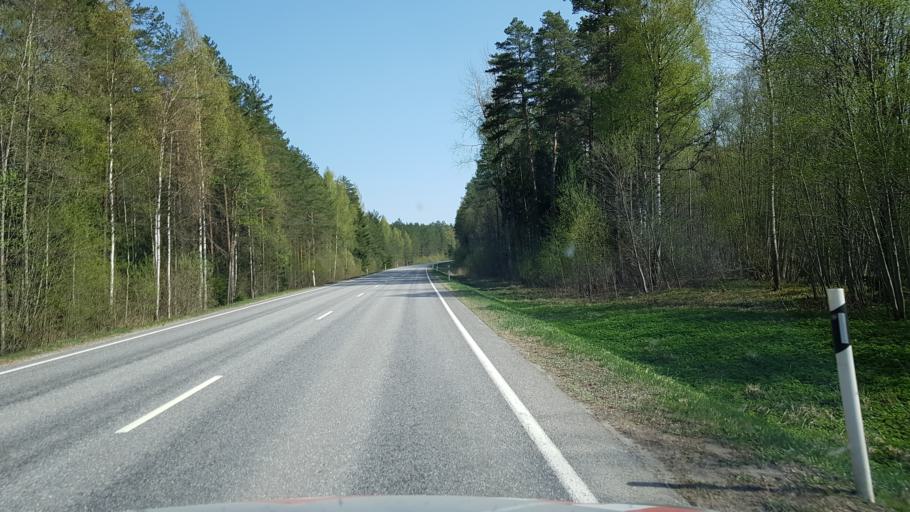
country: EE
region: Paernumaa
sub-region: Saarde vald
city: Kilingi-Nomme
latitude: 58.2103
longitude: 25.0667
